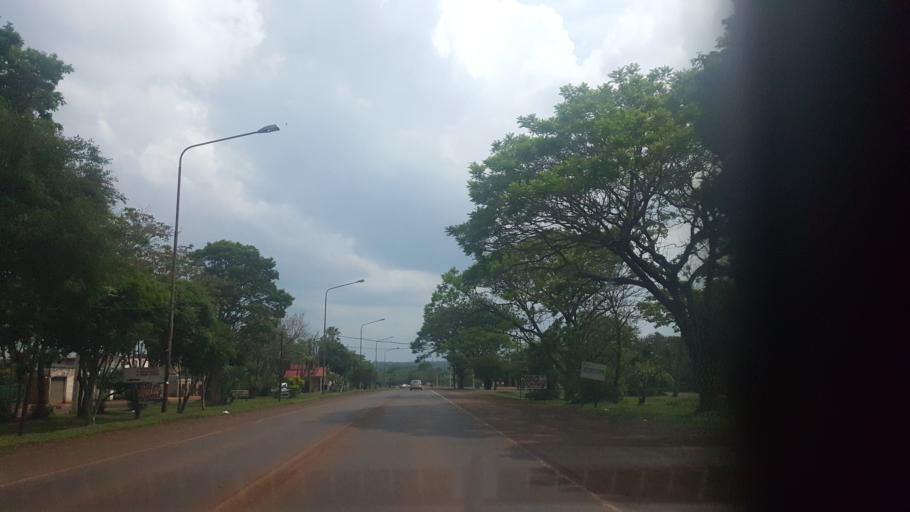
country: AR
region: Misiones
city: Jardin America
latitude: -27.0468
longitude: -55.2421
